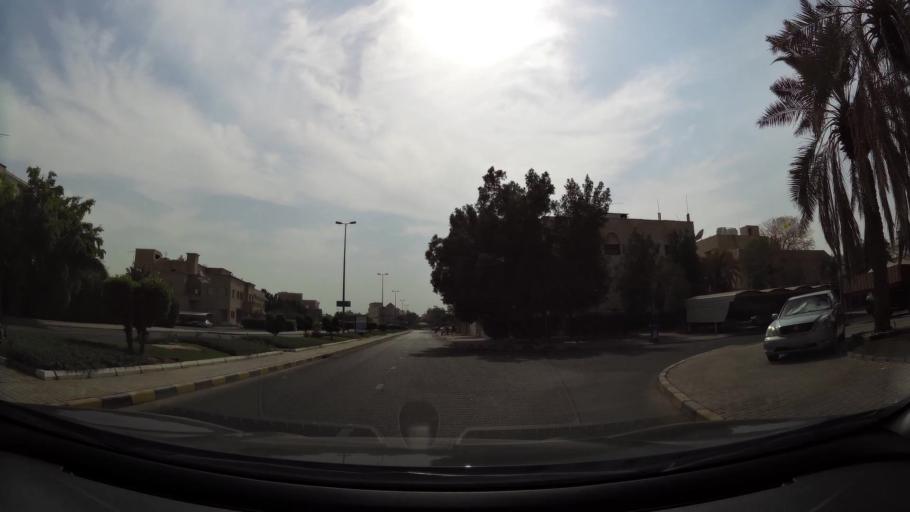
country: KW
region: Al Asimah
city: Ash Shamiyah
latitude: 29.3483
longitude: 47.9626
